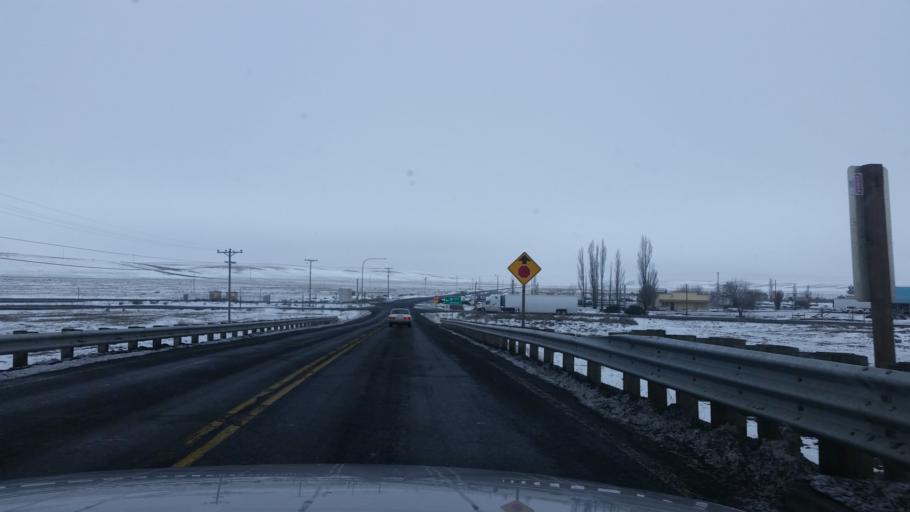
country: US
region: Washington
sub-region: Adams County
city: Ritzville
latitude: 47.2110
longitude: -118.2264
